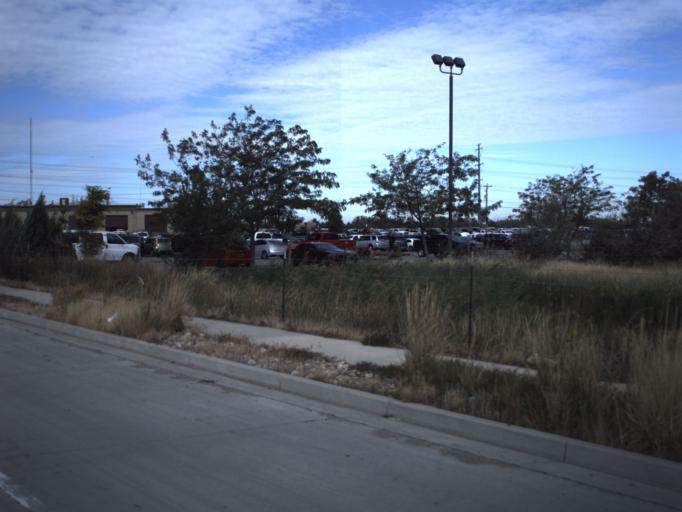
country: US
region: Utah
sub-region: Davis County
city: West Bountiful
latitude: 40.8842
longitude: -111.9241
